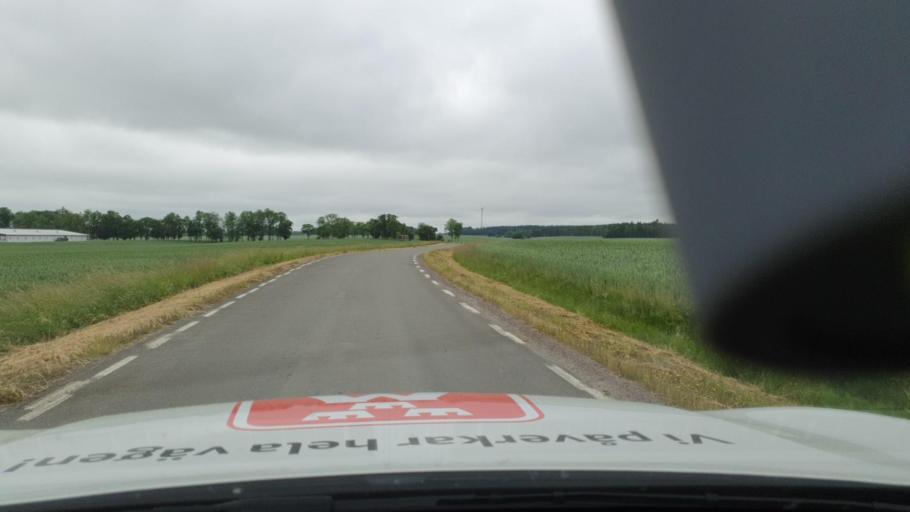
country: SE
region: Vaestra Goetaland
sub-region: Tibro Kommun
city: Tibro
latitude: 58.3719
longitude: 14.1056
